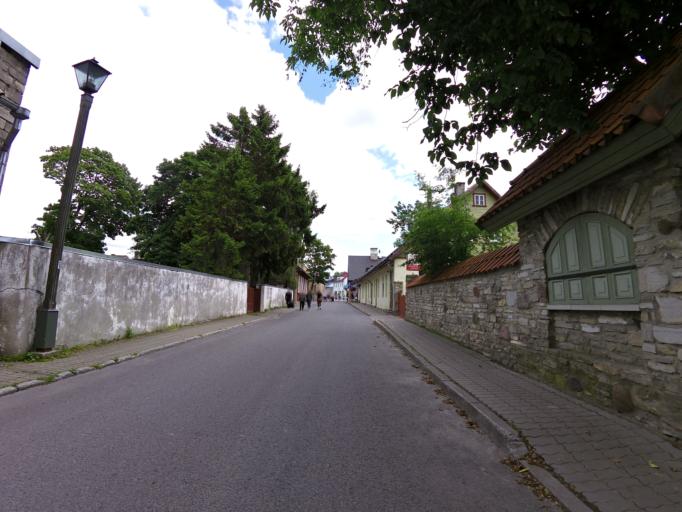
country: EE
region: Laeaene
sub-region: Haapsalu linn
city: Haapsalu
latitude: 58.9486
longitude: 23.5354
